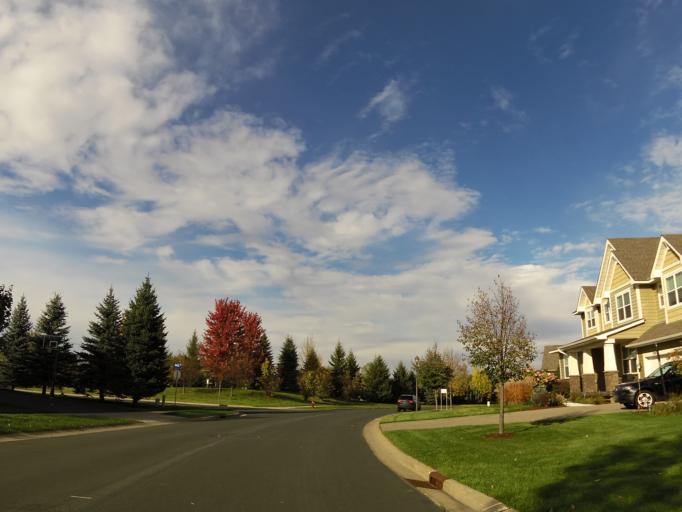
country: US
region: Minnesota
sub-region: Scott County
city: Prior Lake
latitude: 44.7011
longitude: -93.4439
